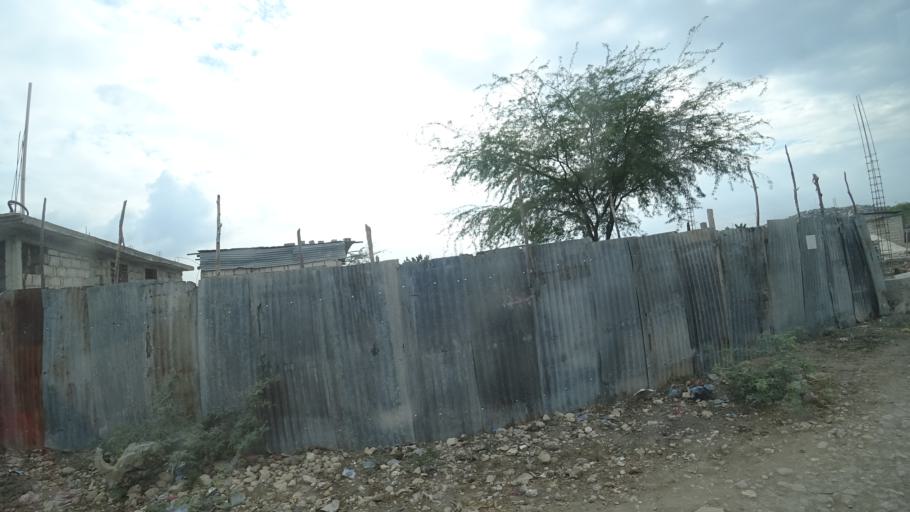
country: HT
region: Ouest
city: Croix des Bouquets
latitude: 18.6574
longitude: -72.2555
